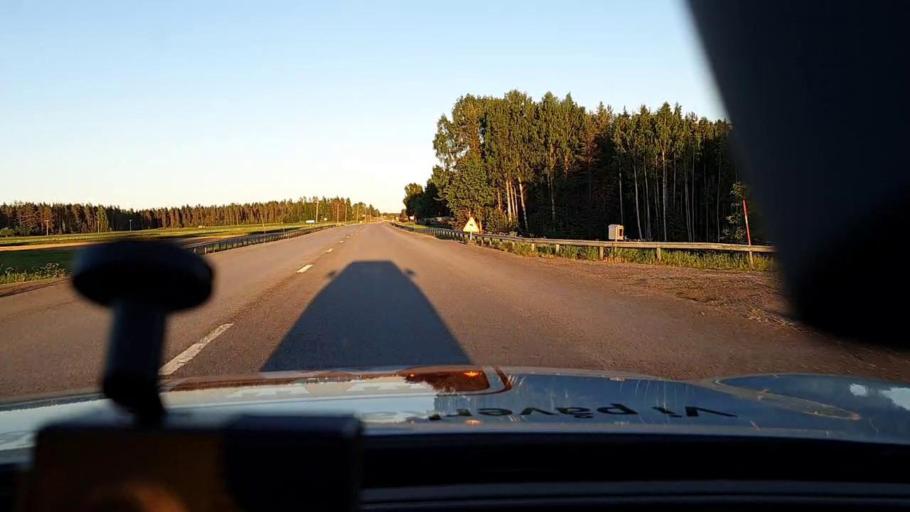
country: SE
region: Norrbotten
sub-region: Bodens Kommun
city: Saevast
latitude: 65.7261
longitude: 21.7845
